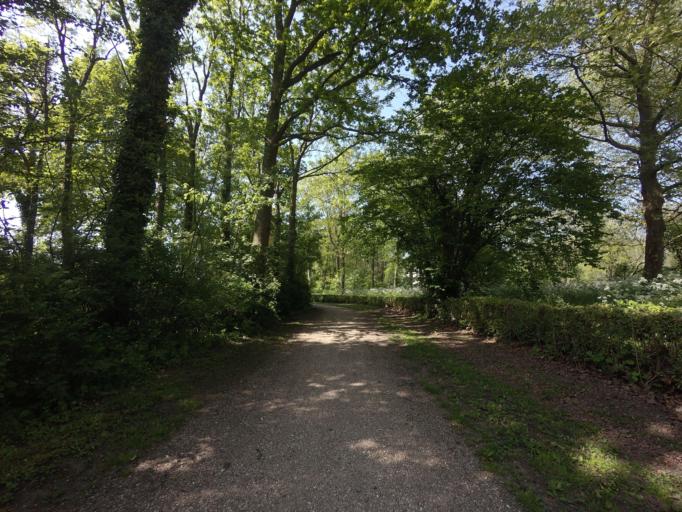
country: NL
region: Zeeland
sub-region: Gemeente Middelburg
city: Middelburg
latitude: 51.5502
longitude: 3.5905
